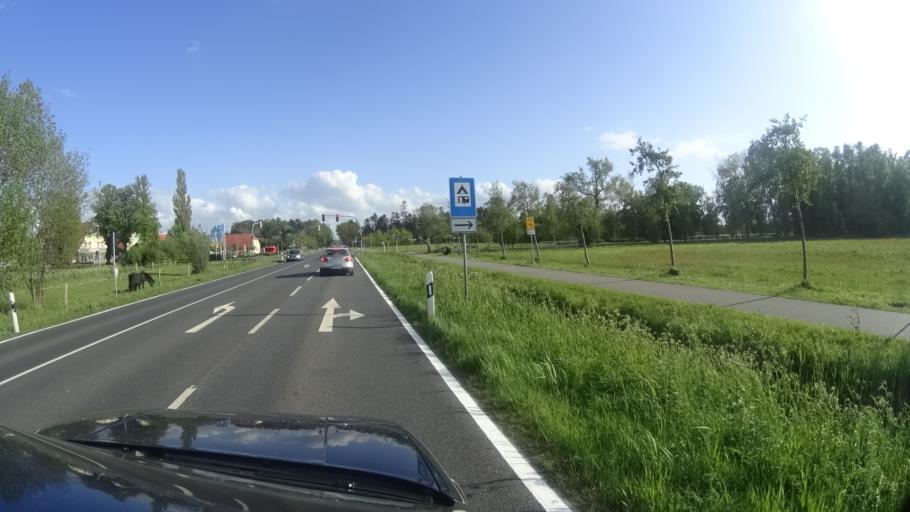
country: DE
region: Mecklenburg-Vorpommern
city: Ostseebad Dierhagen
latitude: 54.2931
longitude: 12.3522
